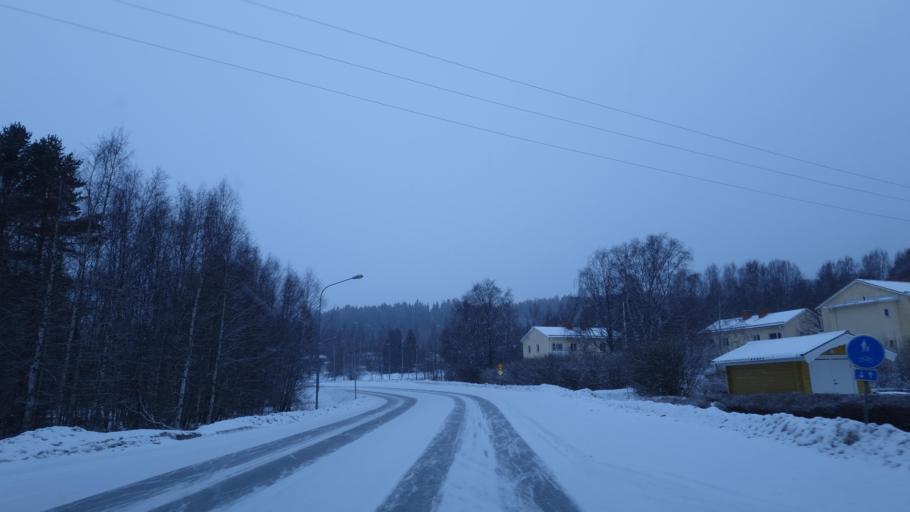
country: SE
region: Vaesternorrland
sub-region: OErnskoeldsviks Kommun
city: Ornskoldsvik
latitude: 63.3004
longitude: 18.6373
